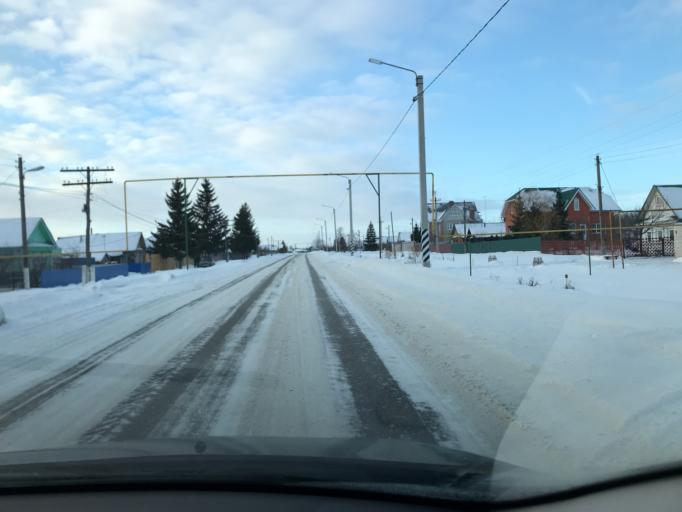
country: RU
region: Ulyanovsk
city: Undory
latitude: 54.6039
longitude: 48.4109
